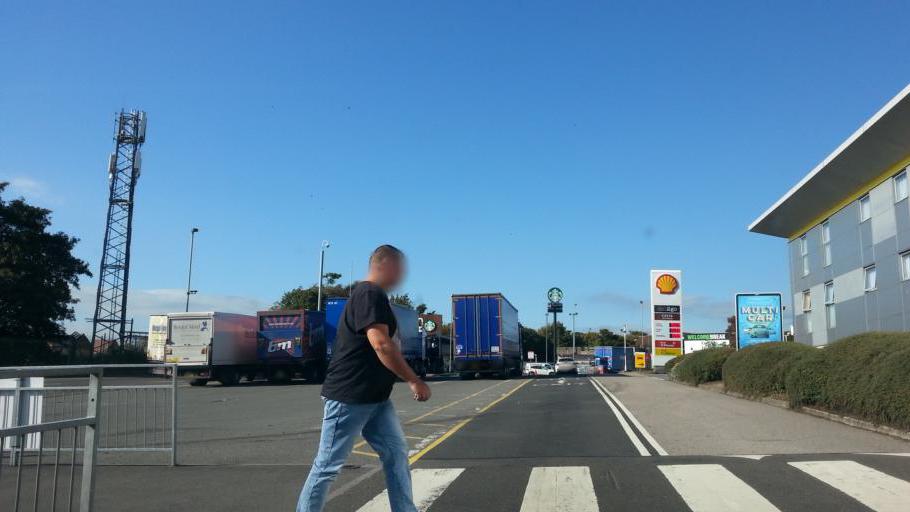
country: GB
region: England
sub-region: Leicestershire
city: Kirby Muxloe
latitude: 52.6185
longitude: -1.2070
